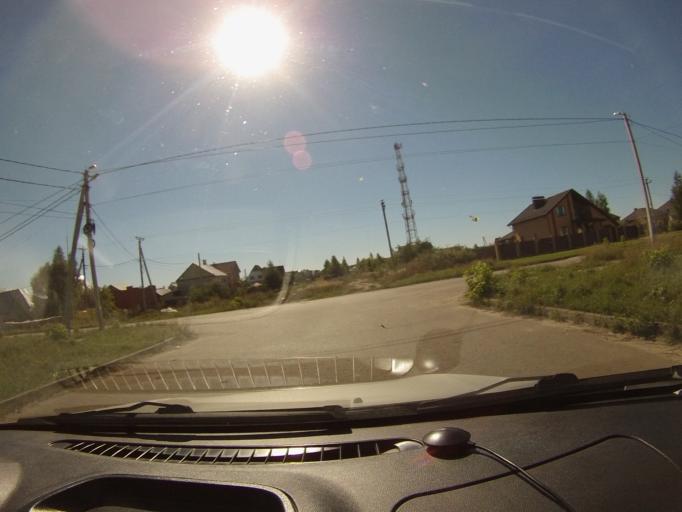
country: RU
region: Tambov
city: Tambov
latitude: 52.7664
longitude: 41.3777
